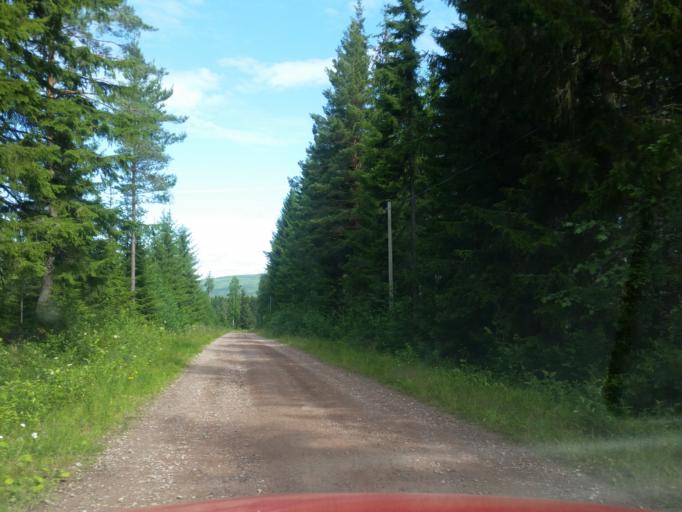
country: SE
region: Dalarna
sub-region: Gagnefs Kommun
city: Gagnef
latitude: 60.6497
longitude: 15.1651
